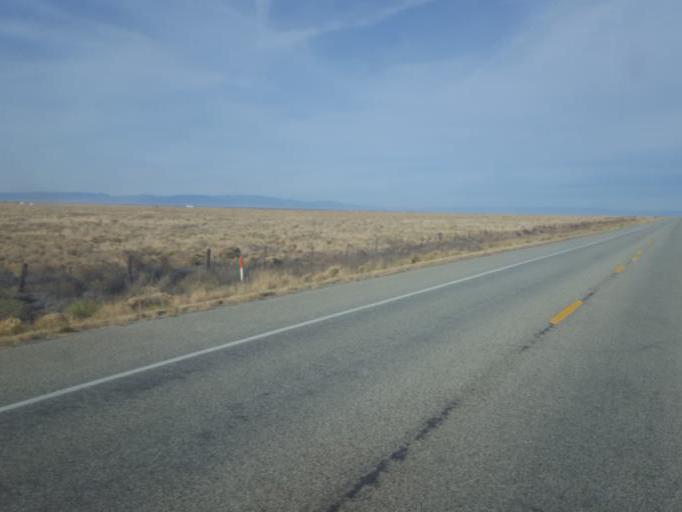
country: US
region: Colorado
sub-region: Alamosa County
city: Alamosa East
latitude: 37.4614
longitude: -105.5612
